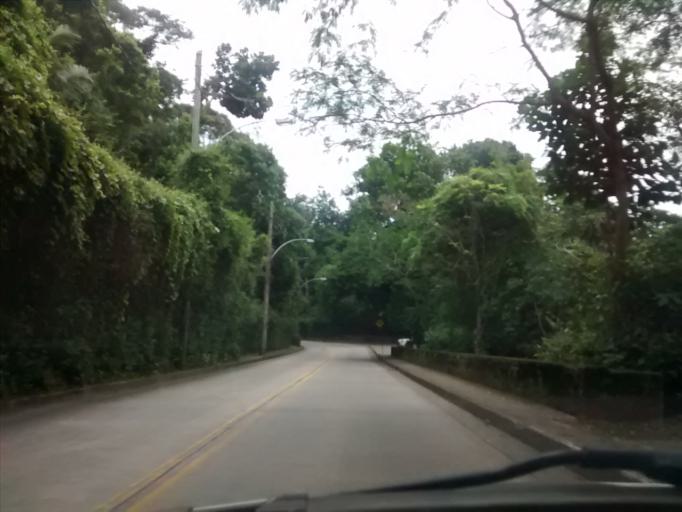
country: BR
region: Rio de Janeiro
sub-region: Rio De Janeiro
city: Rio de Janeiro
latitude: -22.9863
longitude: -43.2708
